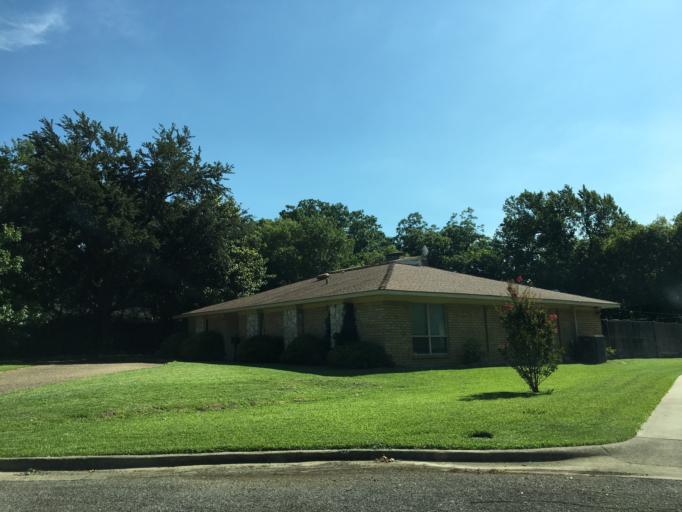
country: US
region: Texas
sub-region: Dallas County
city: Farmers Branch
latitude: 32.9165
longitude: -96.8792
